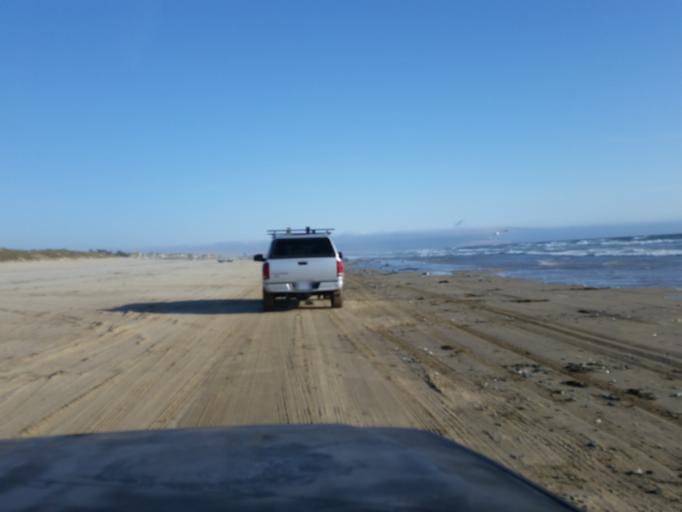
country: US
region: California
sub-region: San Luis Obispo County
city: Grover Beach
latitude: 35.1104
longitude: -120.6330
